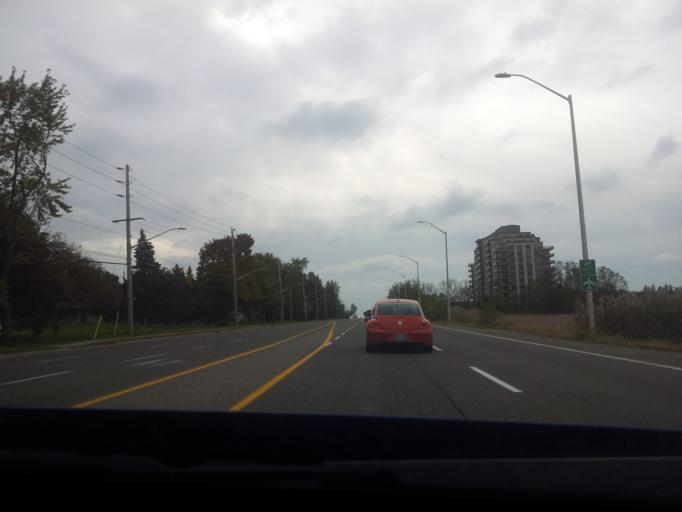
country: CA
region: Ontario
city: London
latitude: 43.0378
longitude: -81.2886
